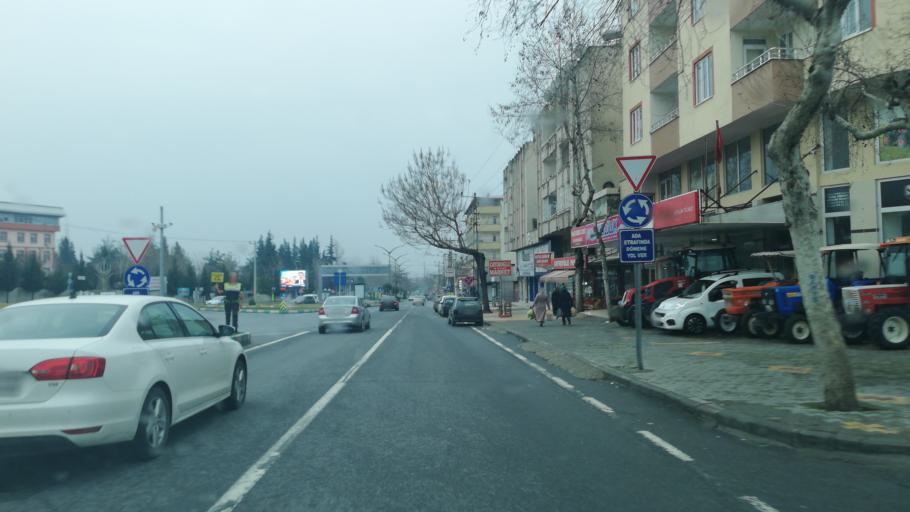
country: TR
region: Kahramanmaras
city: Kahramanmaras
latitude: 37.5669
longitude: 36.9490
